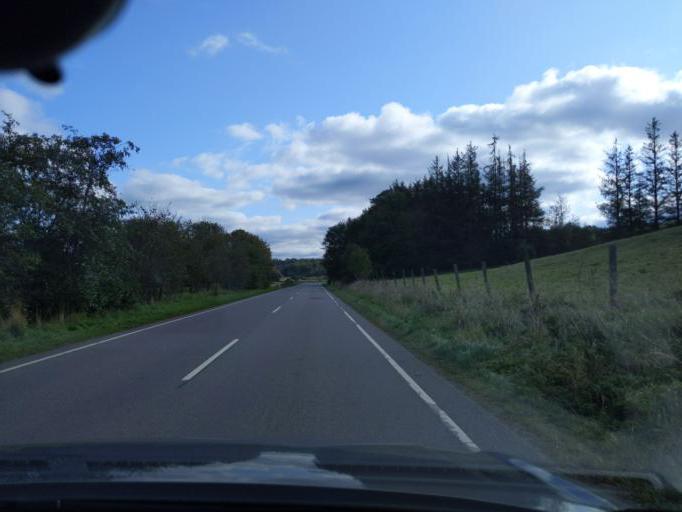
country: DK
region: North Denmark
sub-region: Mariagerfjord Kommune
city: Hobro
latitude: 56.5570
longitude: 9.7260
